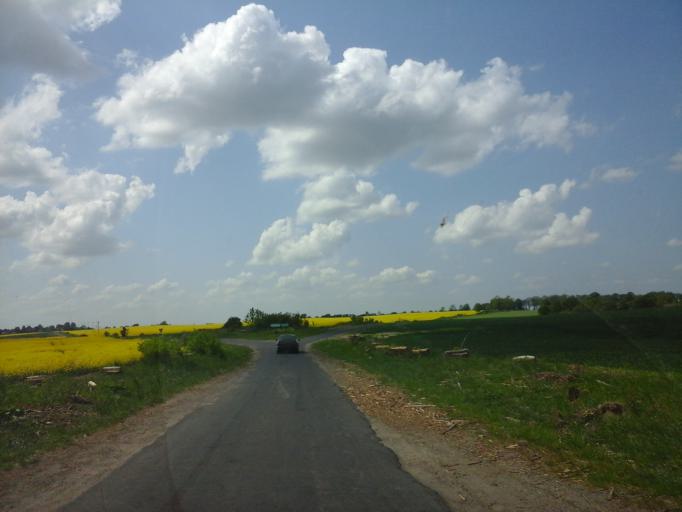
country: PL
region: West Pomeranian Voivodeship
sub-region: Powiat choszczenski
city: Pelczyce
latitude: 53.0493
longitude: 15.2851
